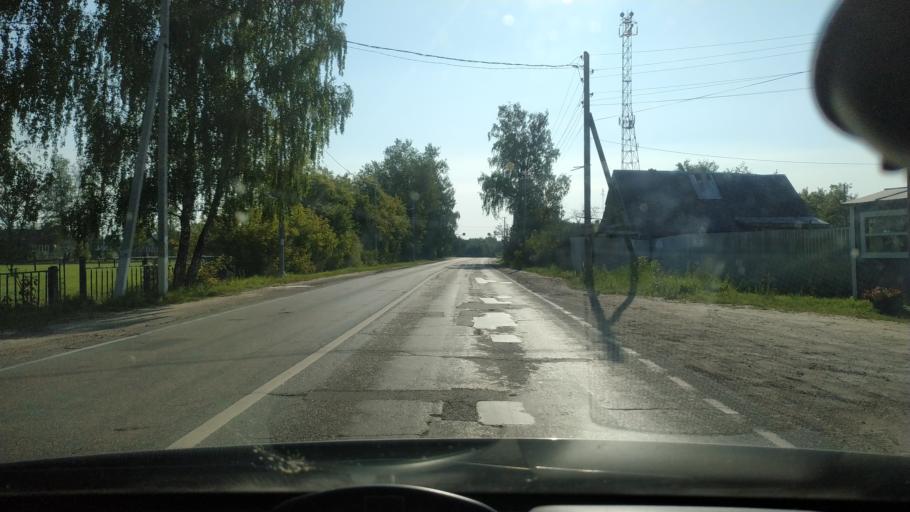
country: RU
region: Moskovskaya
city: Kerva
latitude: 55.5618
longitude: 39.6718
